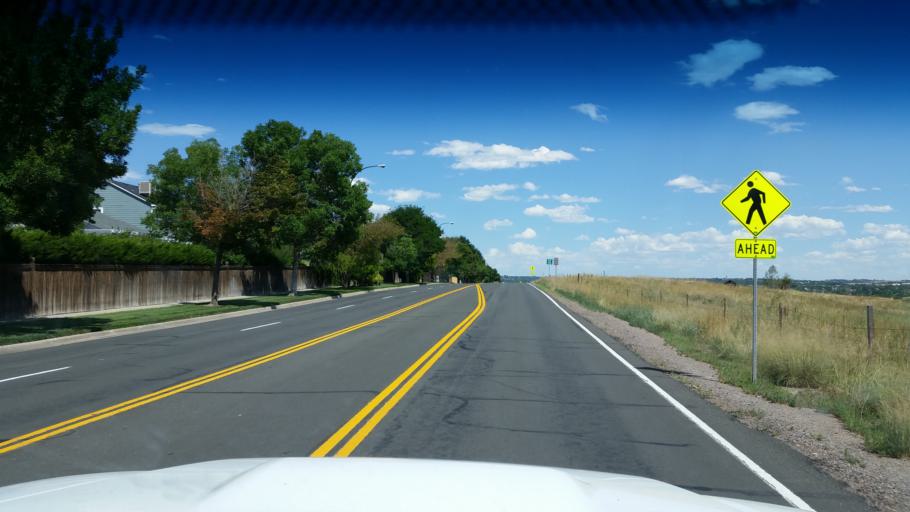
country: US
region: Colorado
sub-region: Broomfield County
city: Broomfield
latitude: 39.8782
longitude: -105.1240
